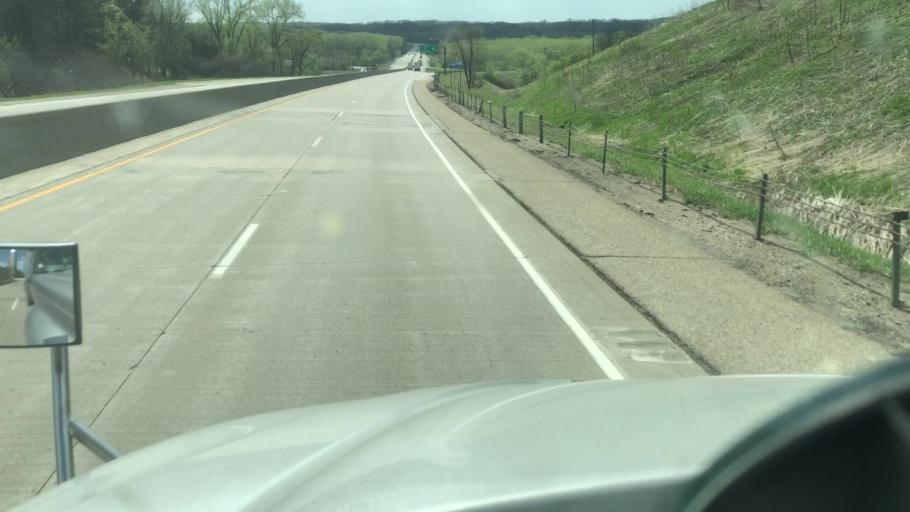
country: US
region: Minnesota
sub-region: Le Sueur County
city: Le Sueur
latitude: 44.4836
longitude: -93.8884
